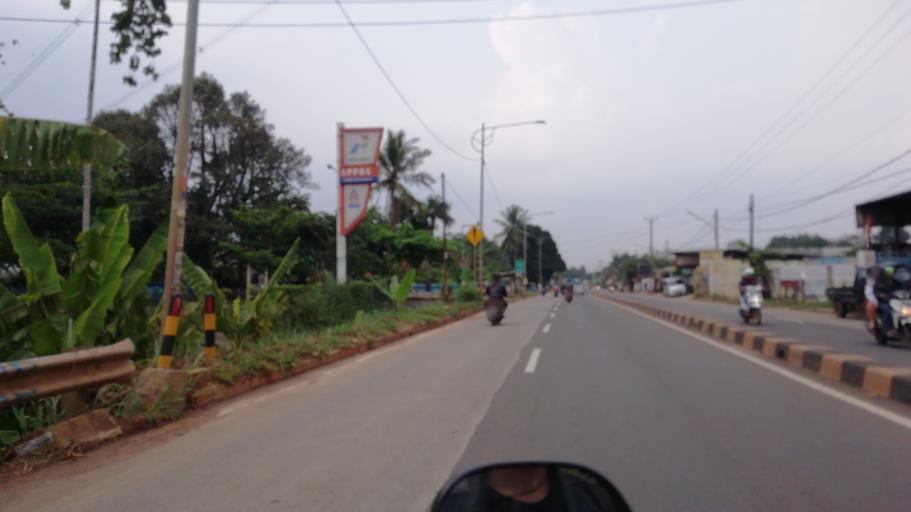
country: ID
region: West Java
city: Parung
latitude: -6.4703
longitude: 106.7292
